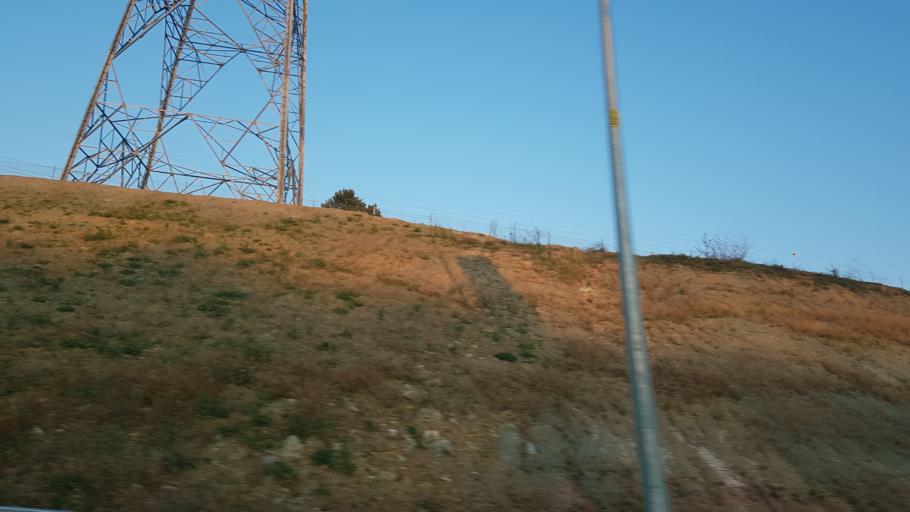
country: TR
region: Kocaeli
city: Tavsanli
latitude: 40.8067
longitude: 29.5199
